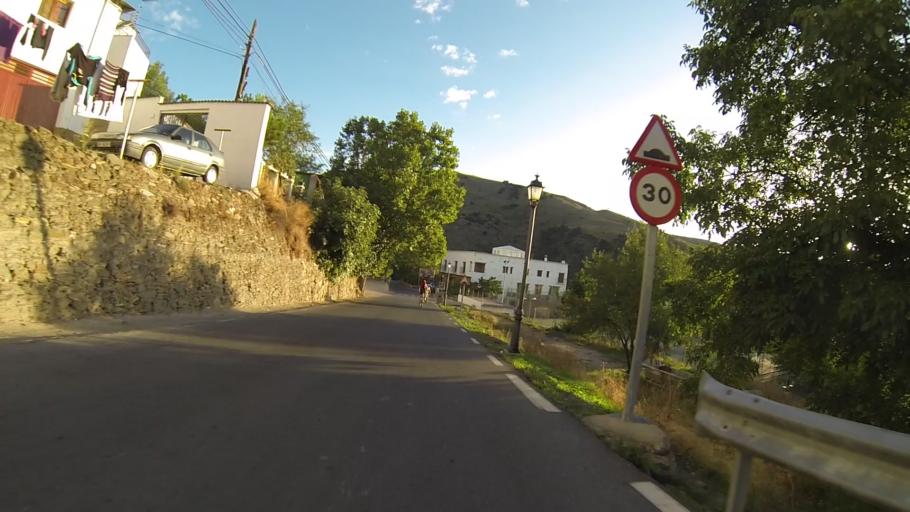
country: ES
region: Andalusia
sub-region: Provincia de Granada
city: Berchules
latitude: 36.9840
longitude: -3.1543
